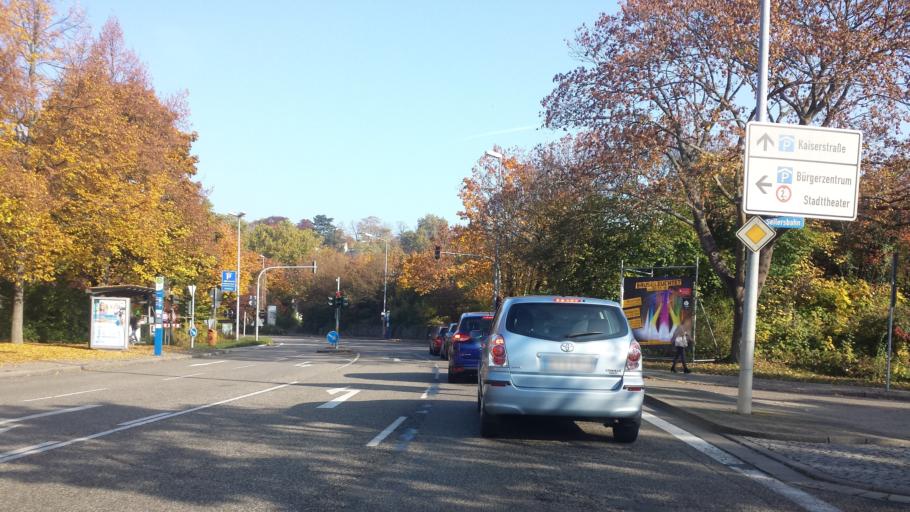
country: DE
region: Baden-Wuerttemberg
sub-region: Karlsruhe Region
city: Bruchsal
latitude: 49.1232
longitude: 8.6008
